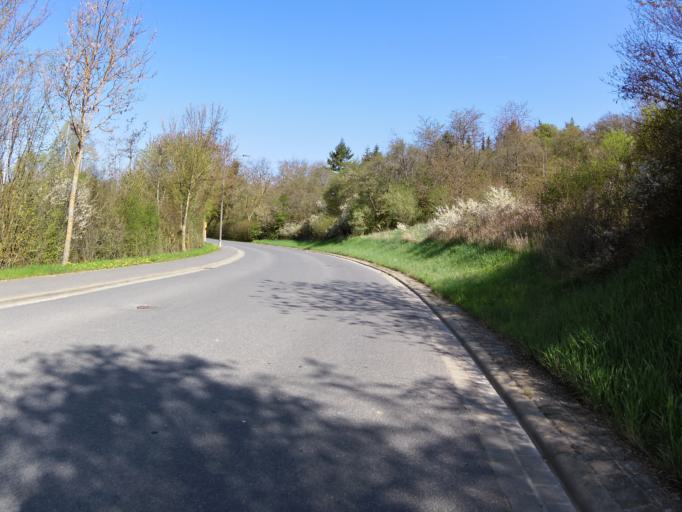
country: DE
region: Bavaria
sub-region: Regierungsbezirk Unterfranken
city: Rottendorf
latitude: 49.7962
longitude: 10.0320
